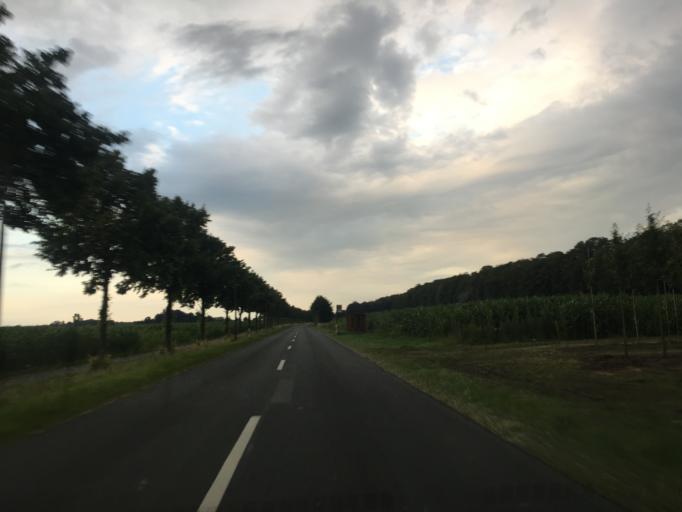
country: DE
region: North Rhine-Westphalia
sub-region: Regierungsbezirk Munster
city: Senden
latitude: 51.8638
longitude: 7.5260
